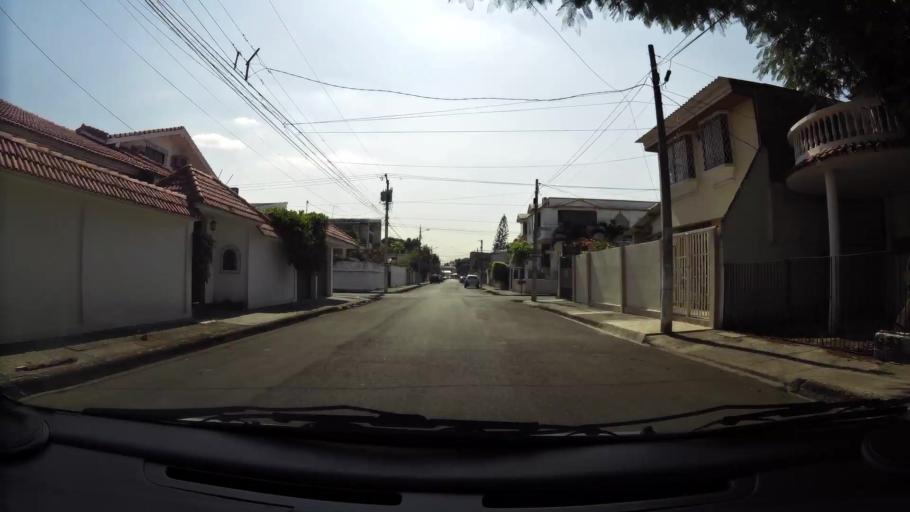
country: EC
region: Guayas
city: Guayaquil
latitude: -2.1663
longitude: -79.9181
